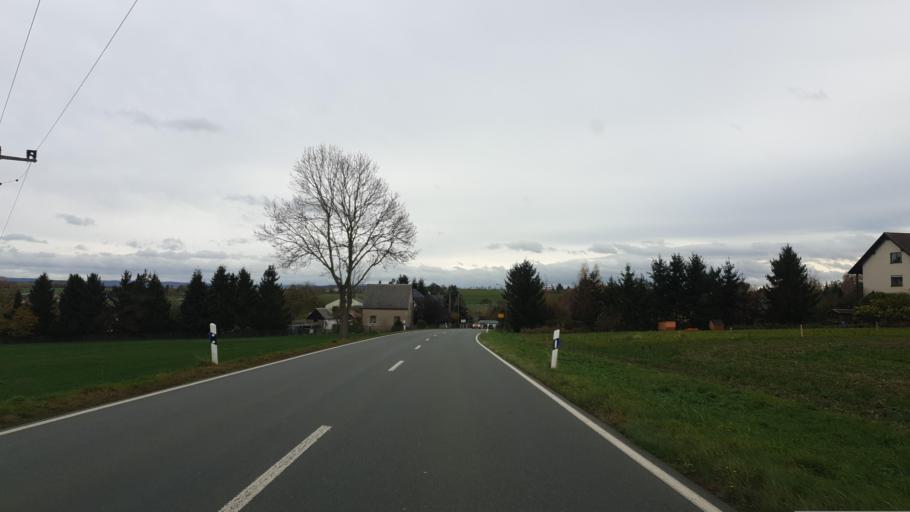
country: DE
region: Saxony
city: Limbach
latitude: 50.5642
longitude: 12.2748
